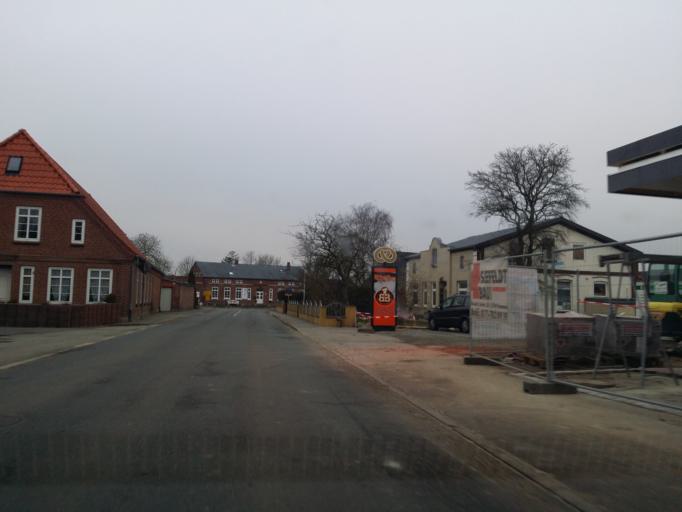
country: DE
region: Schleswig-Holstein
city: Fehmarn
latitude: 54.4515
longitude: 11.1469
